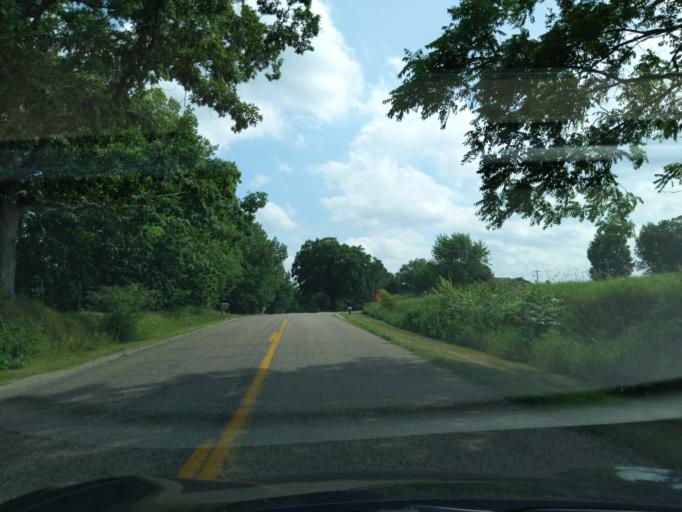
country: US
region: Michigan
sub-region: Eaton County
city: Eaton Rapids
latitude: 42.5158
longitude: -84.6014
